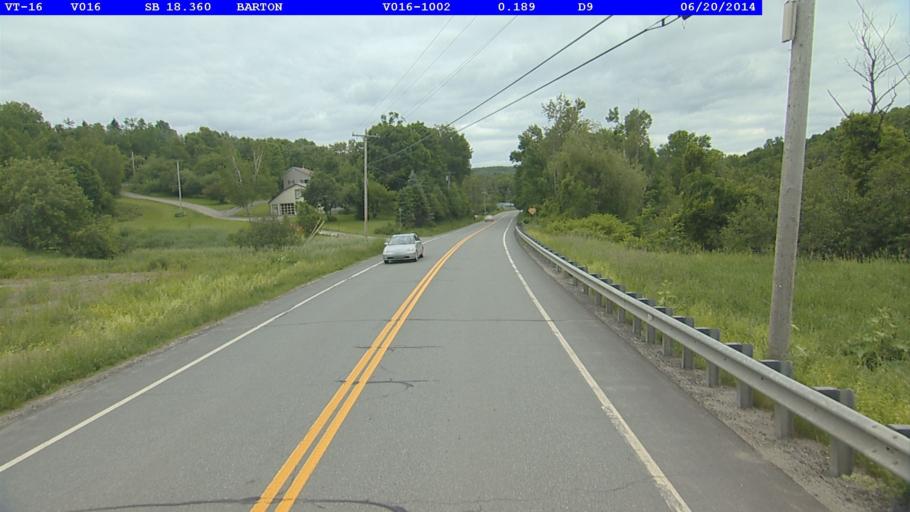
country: US
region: Vermont
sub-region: Orleans County
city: Newport
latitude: 44.7200
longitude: -72.1850
